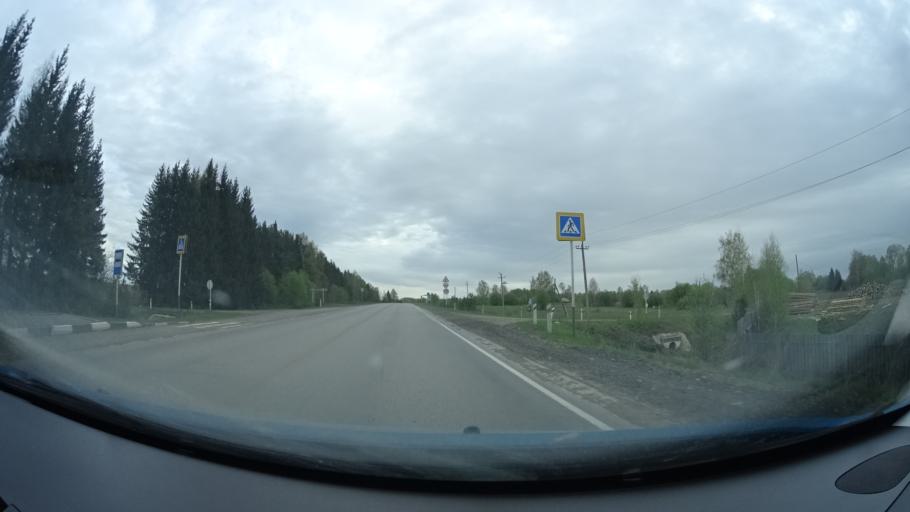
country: RU
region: Perm
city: Osa
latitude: 57.2948
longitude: 55.6116
